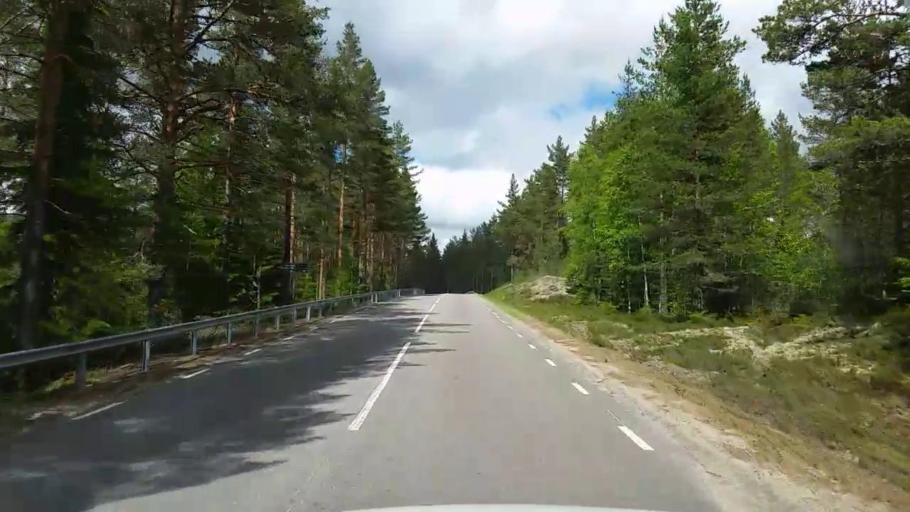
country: SE
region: Gaevleborg
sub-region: Bollnas Kommun
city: Vittsjo
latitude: 61.1324
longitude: 16.1768
